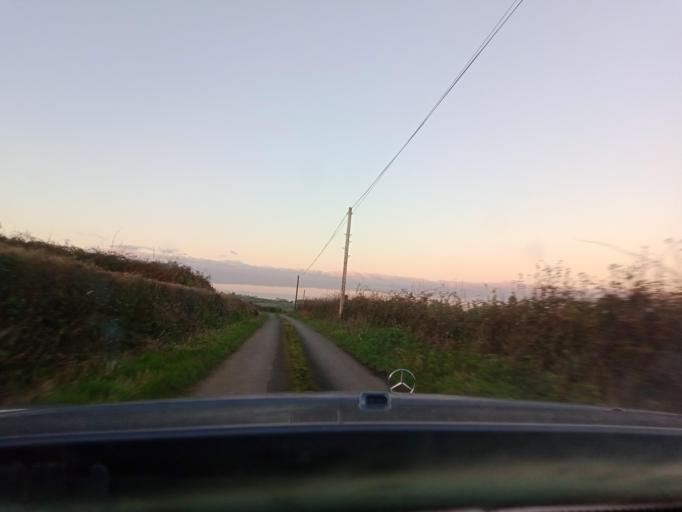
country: IE
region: Leinster
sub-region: Kilkenny
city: Graiguenamanagh
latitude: 52.5609
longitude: -6.9617
